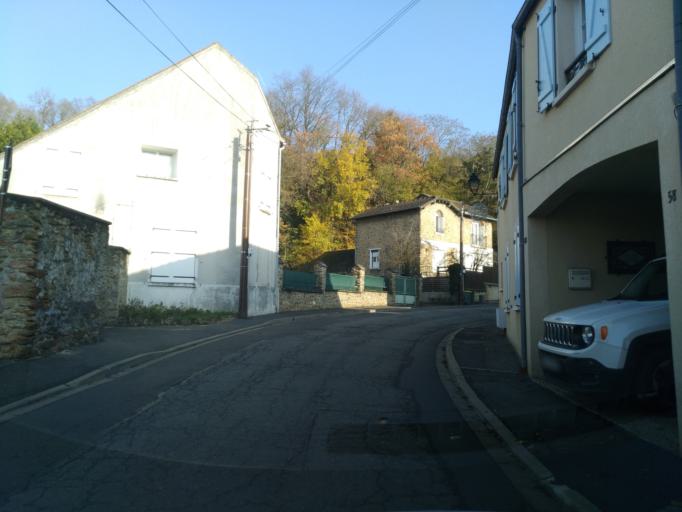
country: FR
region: Ile-de-France
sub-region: Departement des Yvelines
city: Feucherolles
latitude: 48.8745
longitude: 1.9743
